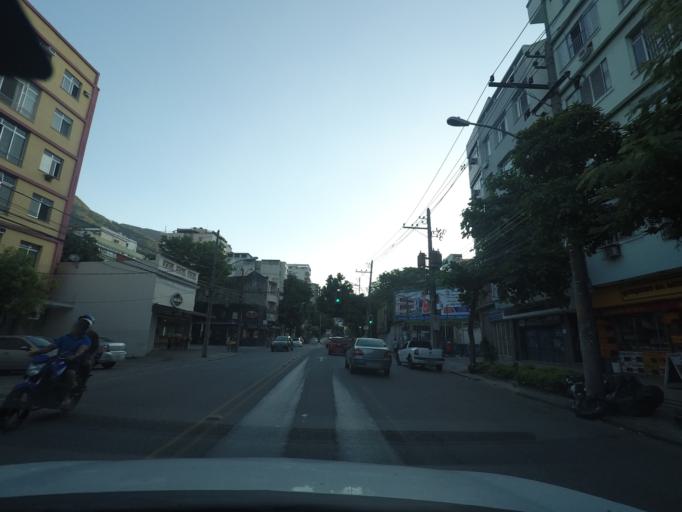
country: BR
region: Rio de Janeiro
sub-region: Rio De Janeiro
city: Rio de Janeiro
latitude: -22.9339
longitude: -43.2423
